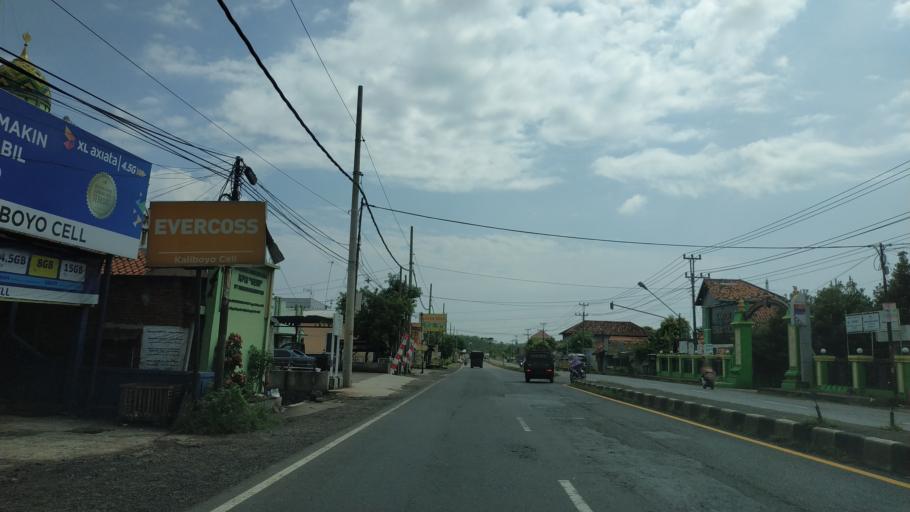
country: ID
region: Central Java
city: Pekalongan
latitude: -6.9497
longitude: 109.8085
